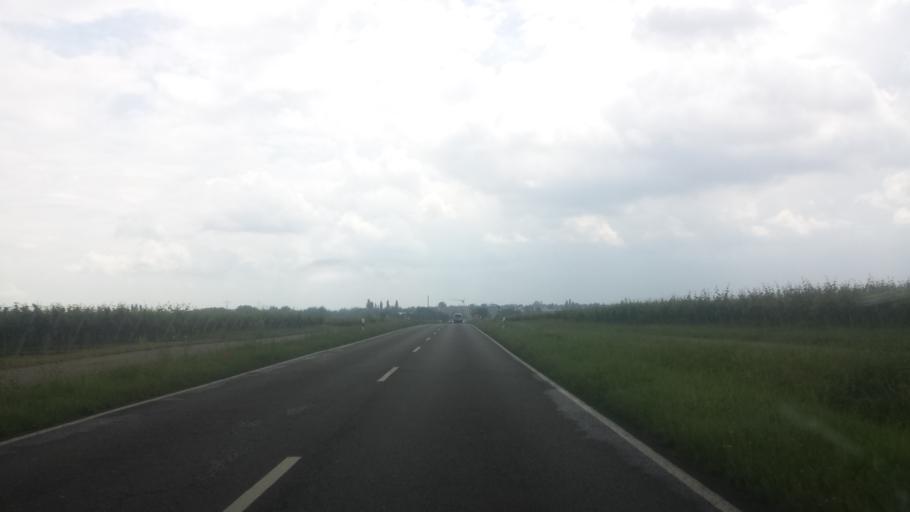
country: DE
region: Rheinland-Pfalz
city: Maikammer
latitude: 49.2968
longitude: 8.1402
